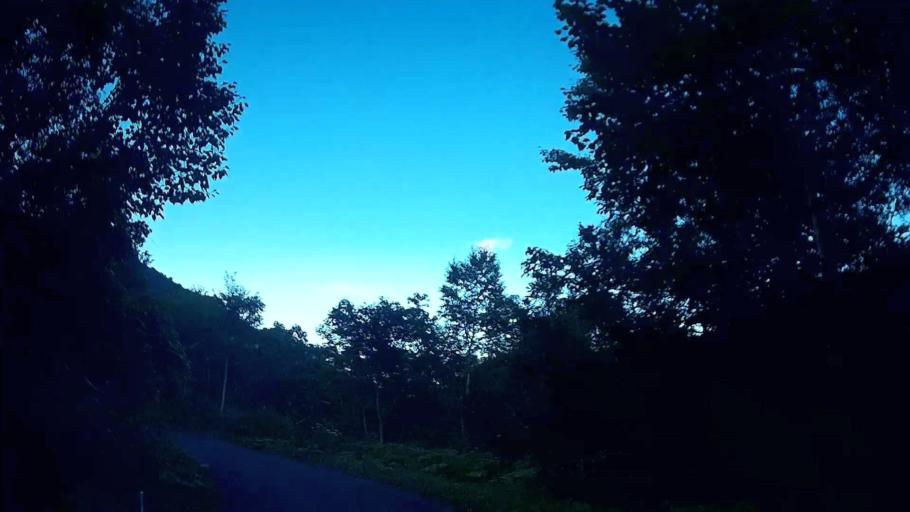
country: JP
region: Hokkaido
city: Iwanai
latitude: 42.5988
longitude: 139.9620
